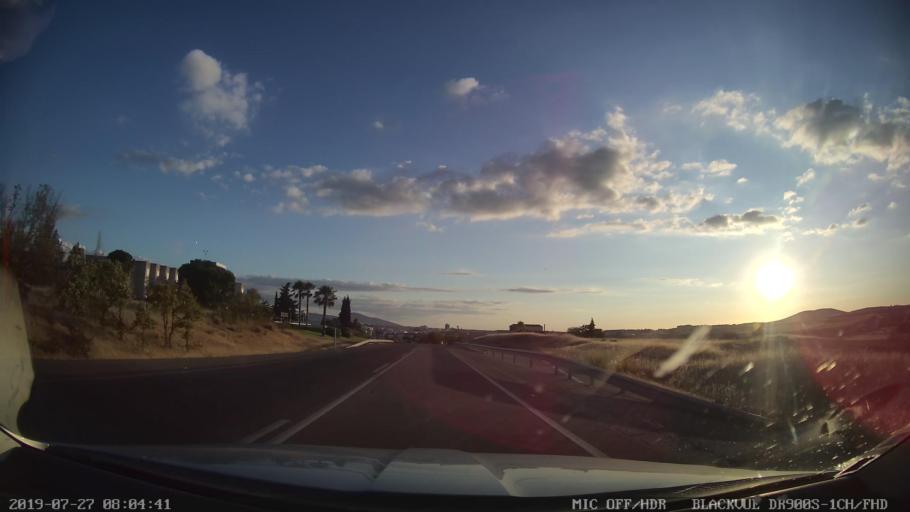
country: ES
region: Extremadura
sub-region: Provincia de Badajoz
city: Merida
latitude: 38.9299
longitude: -6.3153
